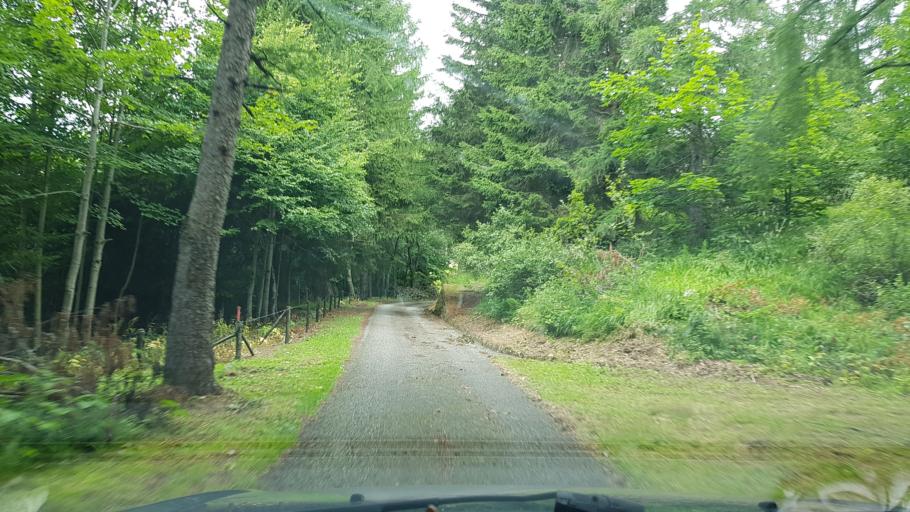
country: IT
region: Friuli Venezia Giulia
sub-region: Provincia di Udine
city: Cercivento
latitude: 46.5476
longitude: 12.9864
